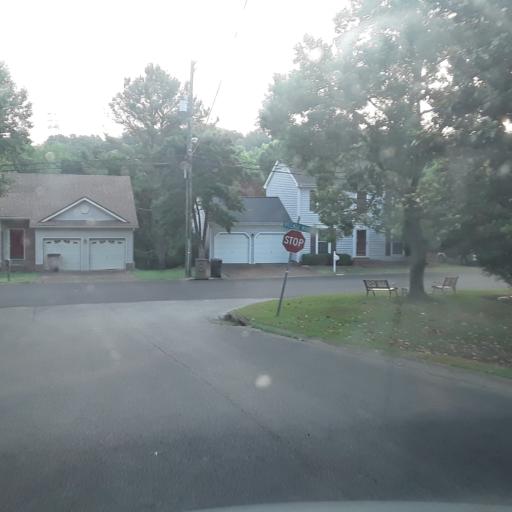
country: US
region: Tennessee
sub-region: Williamson County
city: Brentwood Estates
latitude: 36.0461
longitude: -86.7319
